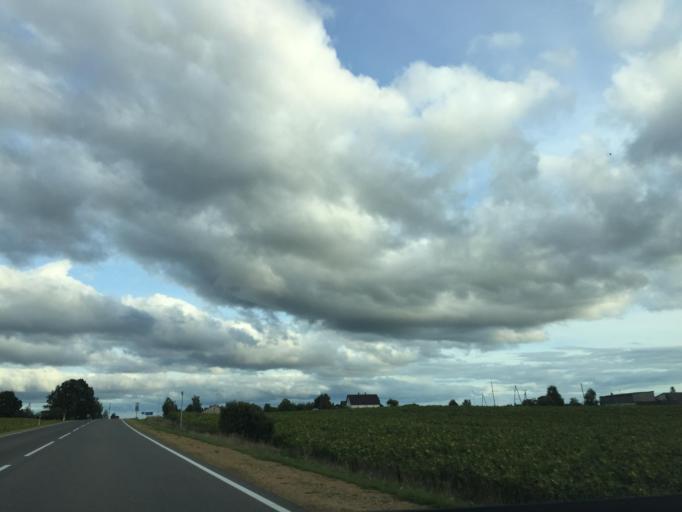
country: LV
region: Nereta
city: Nereta
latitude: 56.2138
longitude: 25.3048
